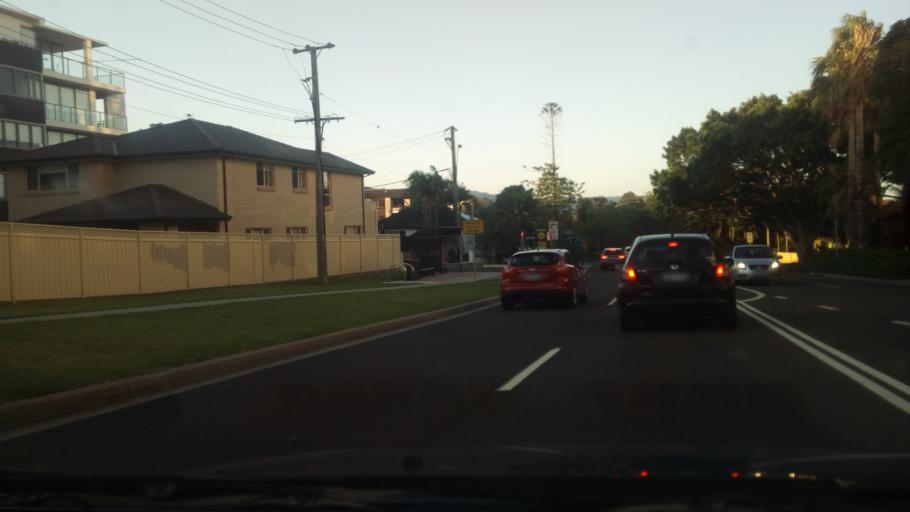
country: AU
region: New South Wales
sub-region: Wollongong
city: Wollongong
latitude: -34.4144
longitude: 150.8996
